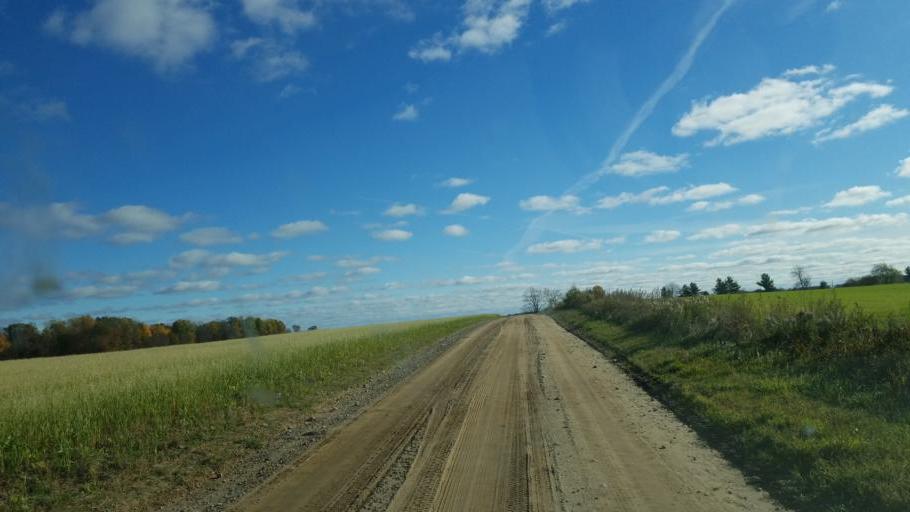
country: US
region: Michigan
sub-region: Montcalm County
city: Edmore
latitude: 43.4660
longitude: -85.0395
